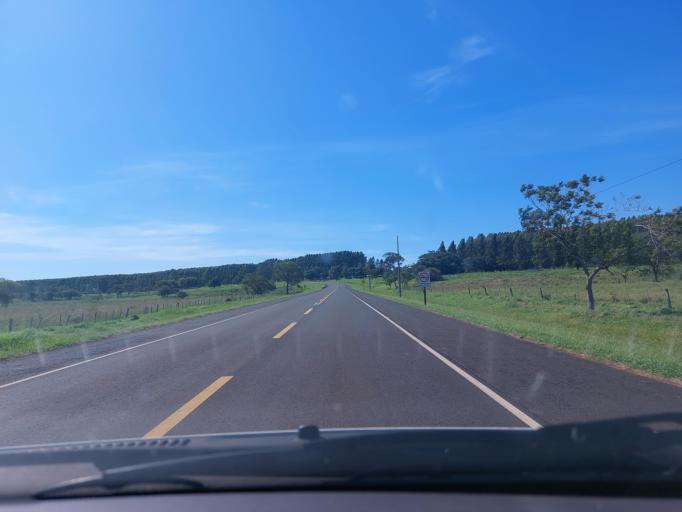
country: PY
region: San Pedro
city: Itacurubi del Rosario
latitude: -24.6036
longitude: -56.7664
